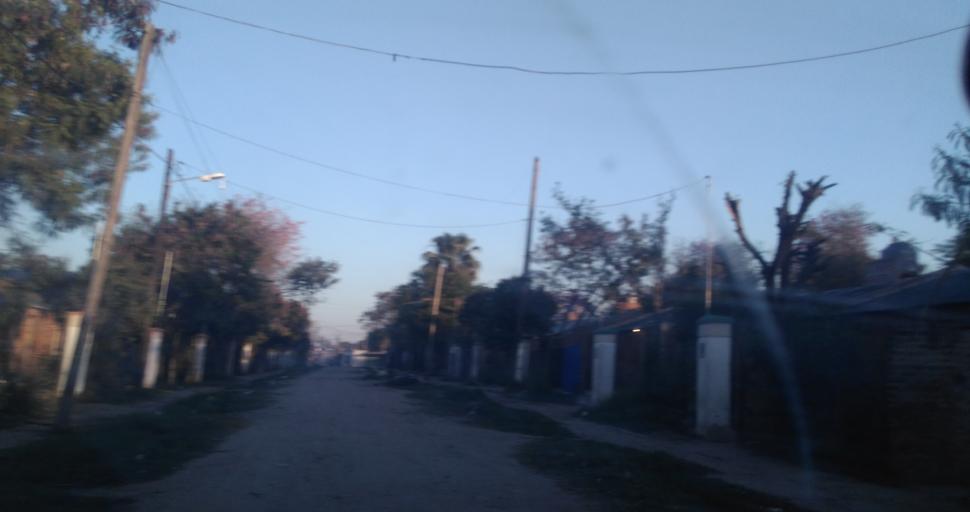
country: AR
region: Chaco
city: Fontana
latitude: -27.4244
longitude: -59.0281
